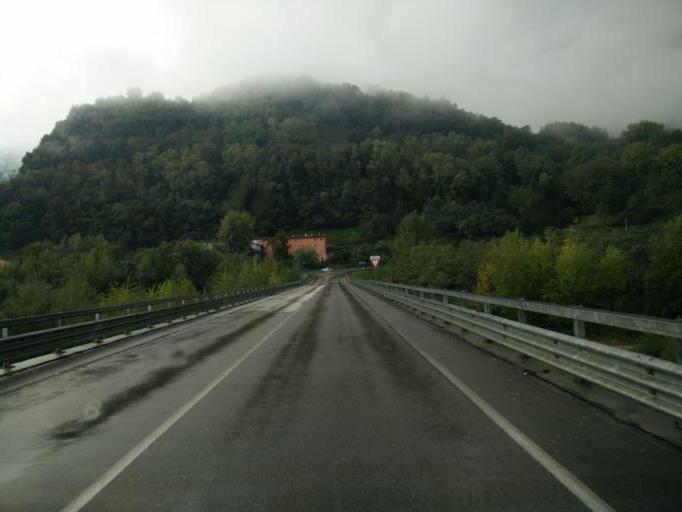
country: IT
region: Tuscany
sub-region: Provincia di Lucca
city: Piano di Coreglia-Ghivizzano
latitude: 44.0332
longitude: 10.4918
